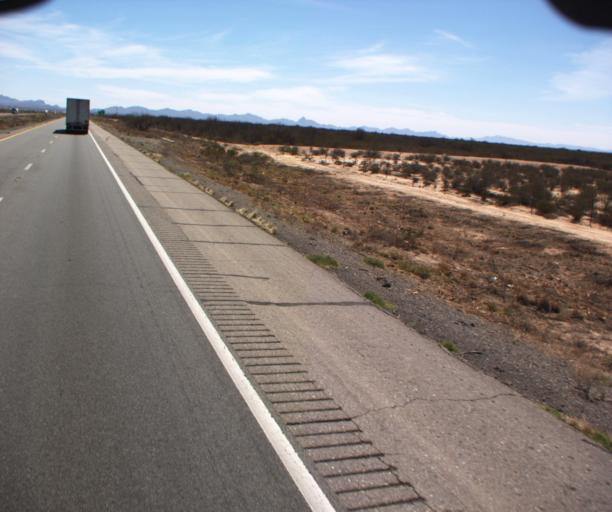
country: US
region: Arizona
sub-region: Cochise County
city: Willcox
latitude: 32.2803
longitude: -109.2804
